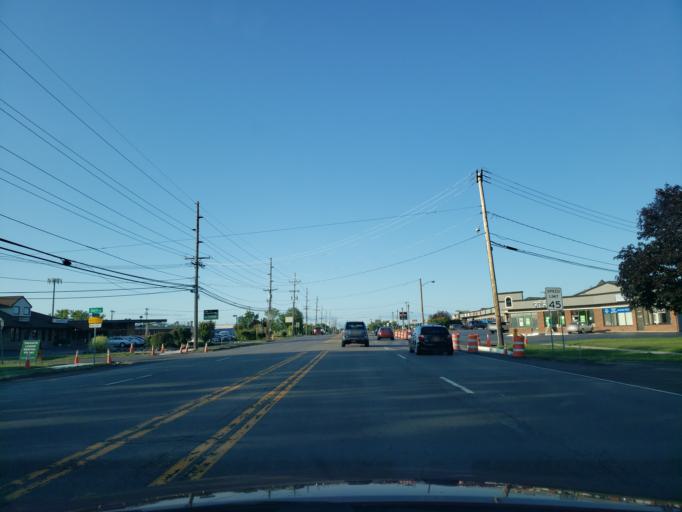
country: US
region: New York
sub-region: Monroe County
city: Brighton
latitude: 43.1859
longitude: -77.5060
